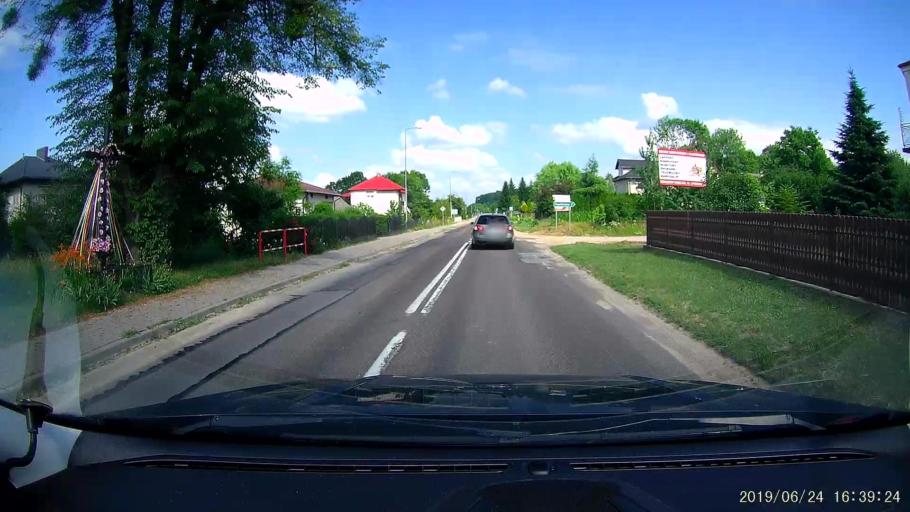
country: PL
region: Lublin Voivodeship
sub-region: Powiat tomaszowski
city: Rachanie
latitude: 50.5298
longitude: 23.5546
